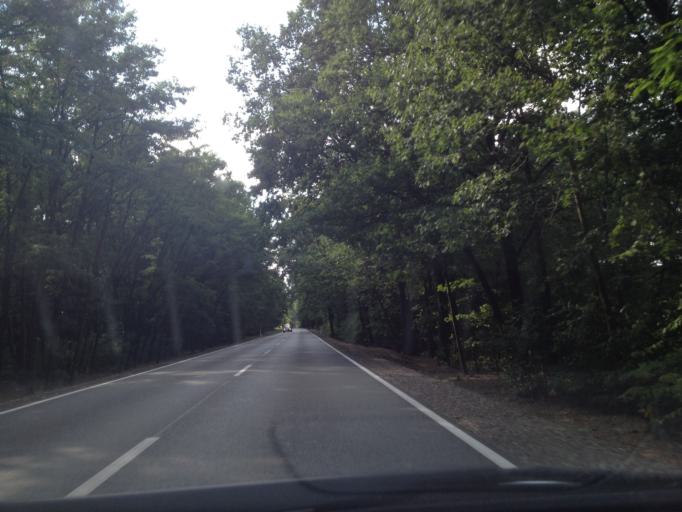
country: PL
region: Lubusz
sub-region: Powiat zarski
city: Sieniawa Zarska
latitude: 51.6325
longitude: 15.0310
